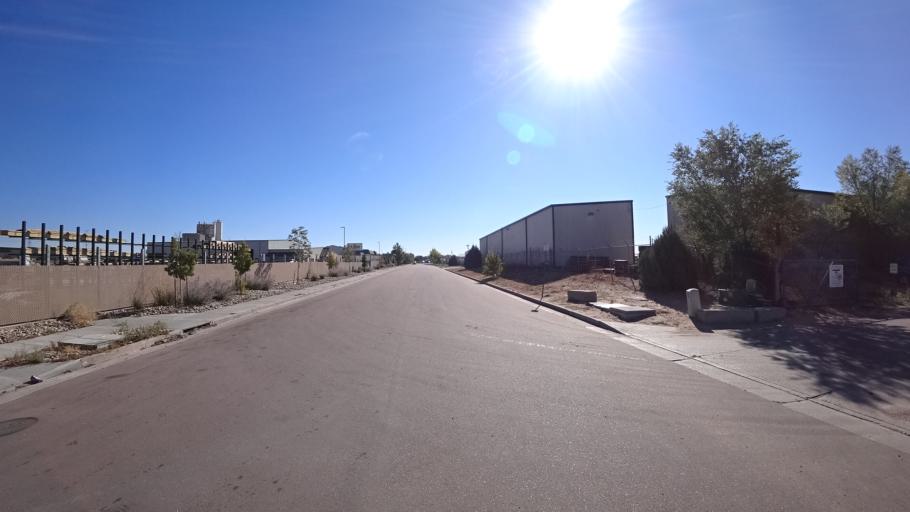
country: US
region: Colorado
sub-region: El Paso County
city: Stratmoor
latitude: 38.7860
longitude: -104.7693
